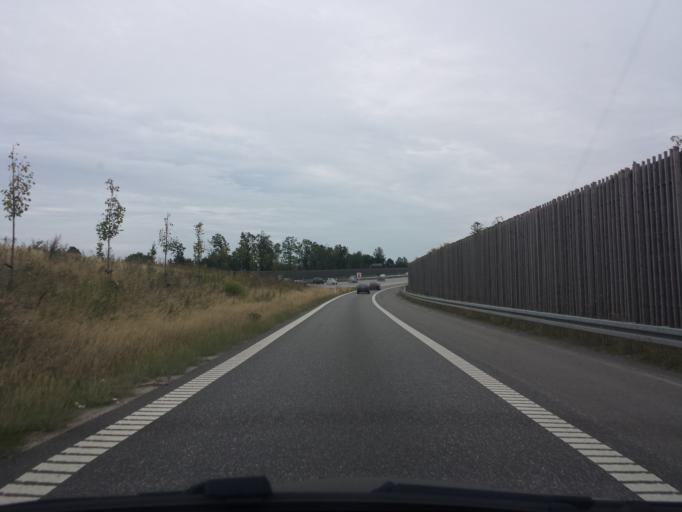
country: DK
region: Capital Region
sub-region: Hoje-Taastrup Kommune
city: Flong
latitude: 55.6547
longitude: 12.1794
